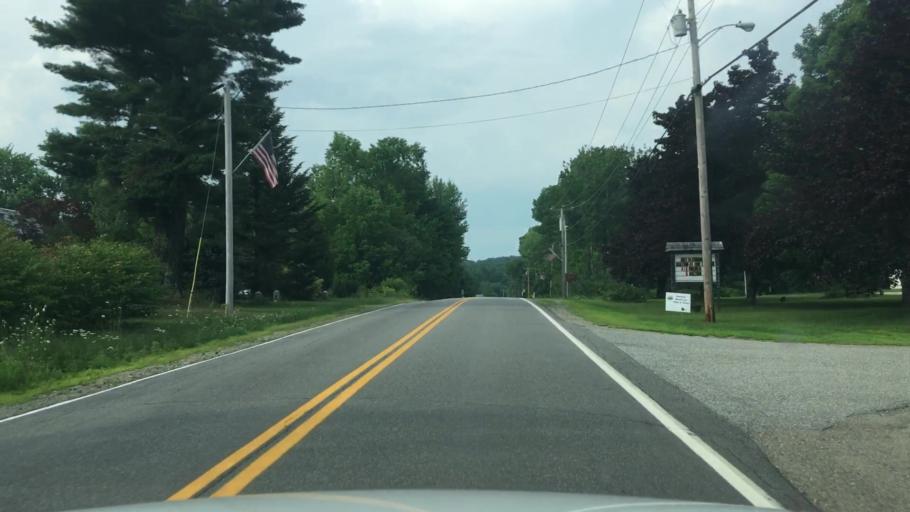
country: US
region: Maine
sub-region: Knox County
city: Washington
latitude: 44.2672
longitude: -69.3724
